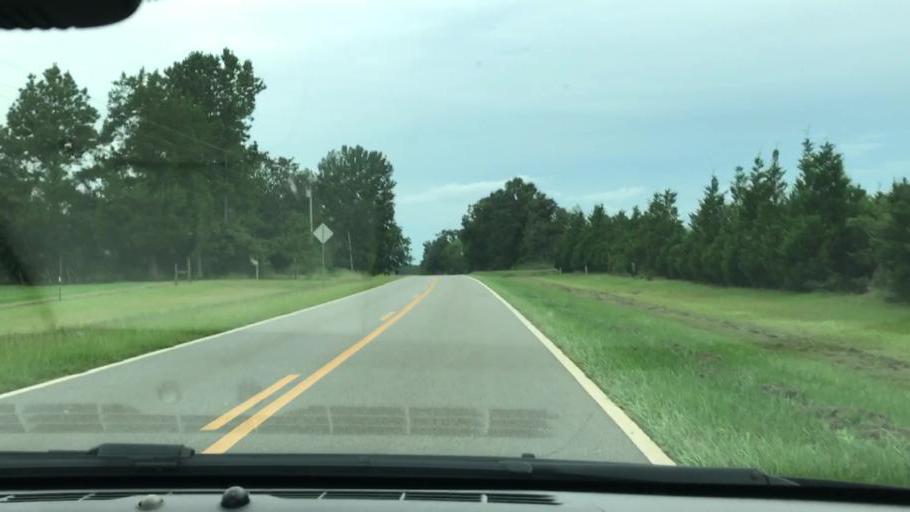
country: US
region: Georgia
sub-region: Early County
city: Blakely
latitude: 31.4369
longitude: -84.9186
